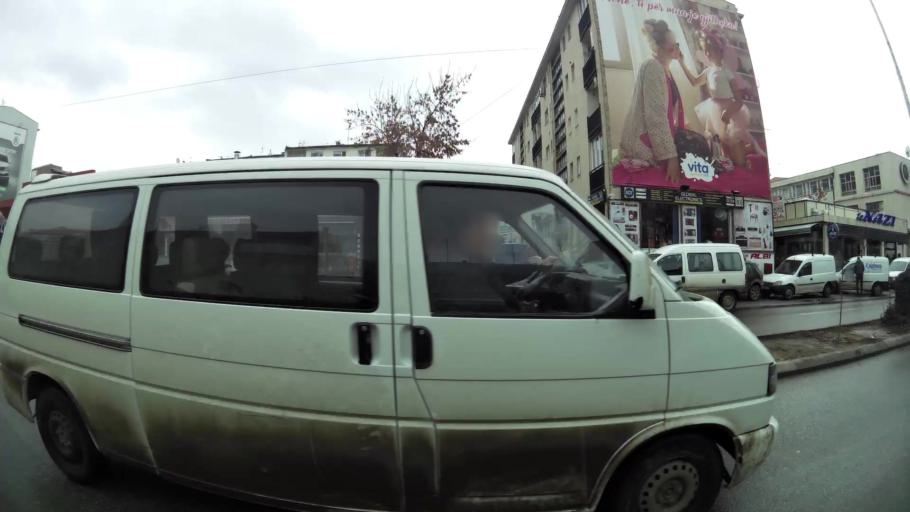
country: XK
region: Pristina
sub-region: Komuna e Prishtines
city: Pristina
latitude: 42.6545
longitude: 21.1593
